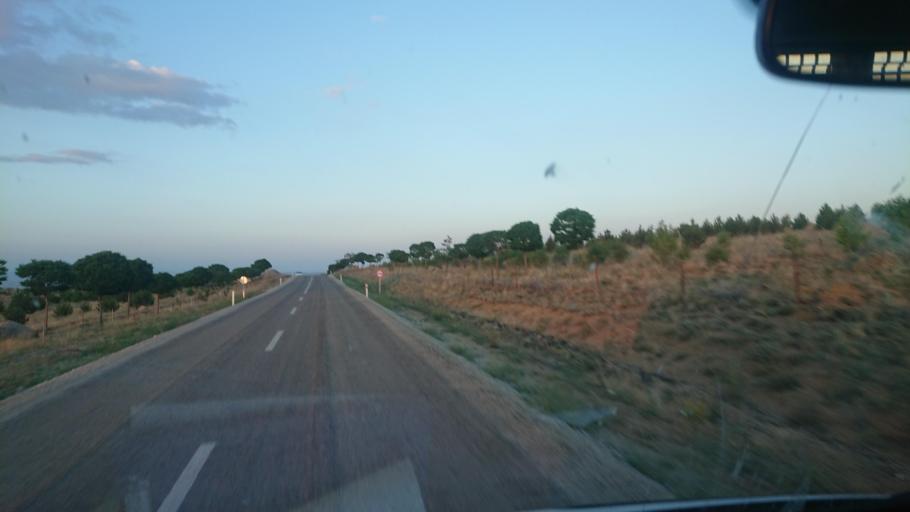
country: TR
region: Aksaray
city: Sariyahsi
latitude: 38.9695
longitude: 33.8044
